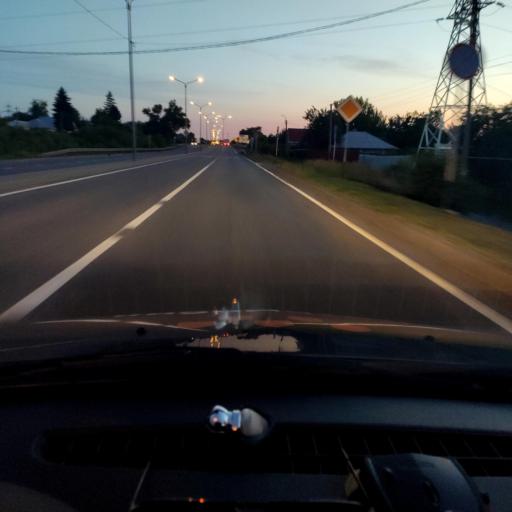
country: RU
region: Belgorod
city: Gubkin
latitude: 51.2709
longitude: 37.5771
